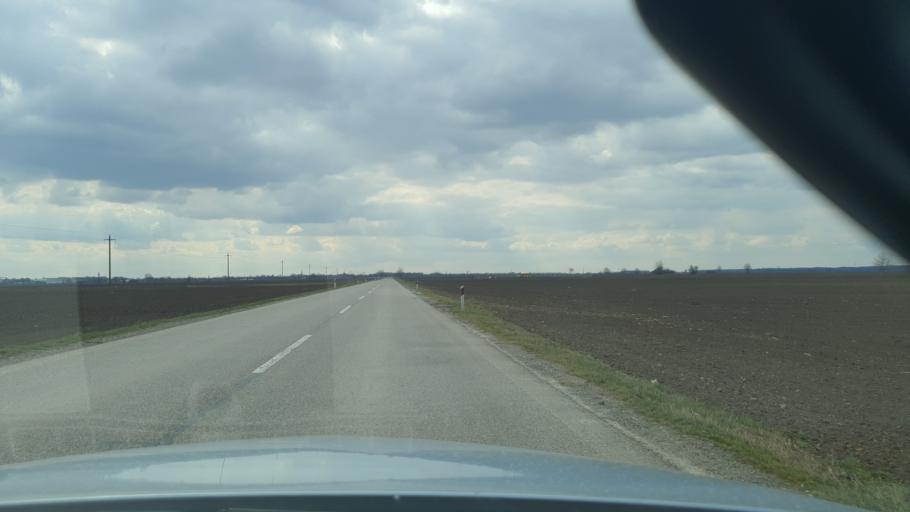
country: RS
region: Autonomna Pokrajina Vojvodina
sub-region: Zapadnobacki Okrug
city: Odzaci
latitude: 45.4370
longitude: 19.3135
